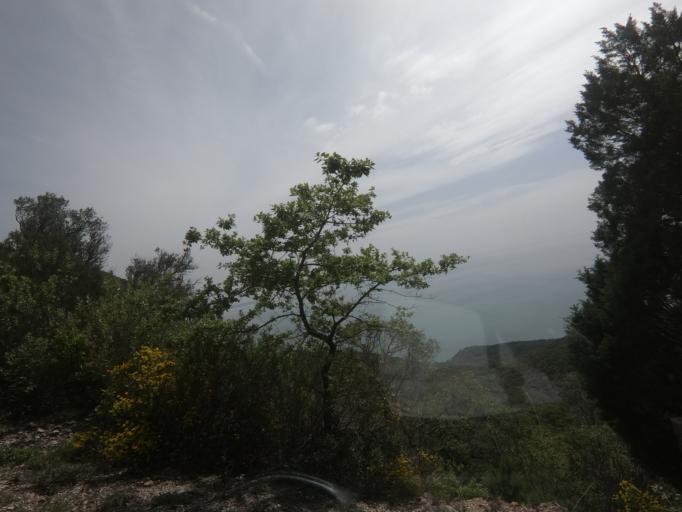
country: PT
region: Setubal
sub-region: Palmela
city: Quinta do Anjo
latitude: 38.4786
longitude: -8.9935
